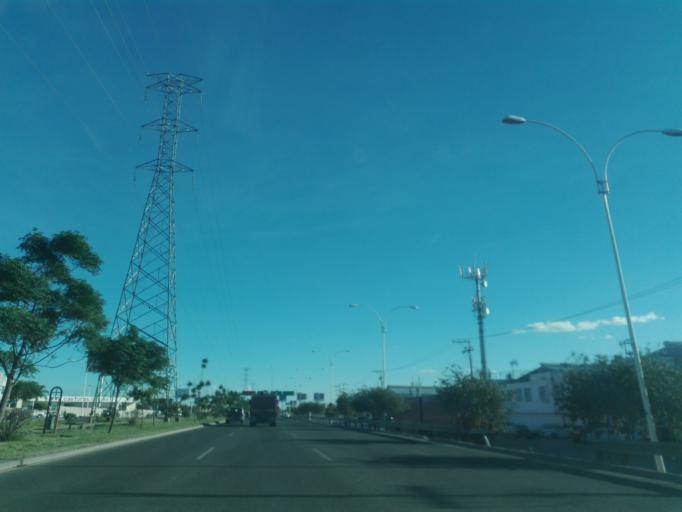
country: MX
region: Guanajuato
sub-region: Leon
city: Medina
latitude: 21.1196
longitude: -101.6272
